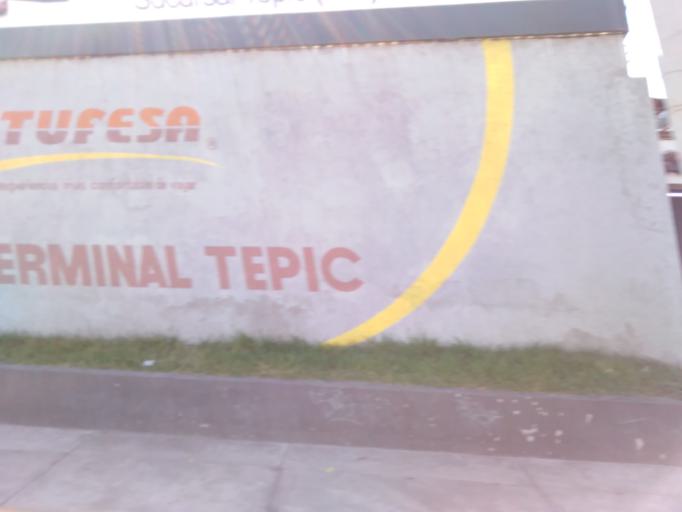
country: MX
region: Nayarit
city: Xalisco
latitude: 21.4757
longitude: -104.8640
